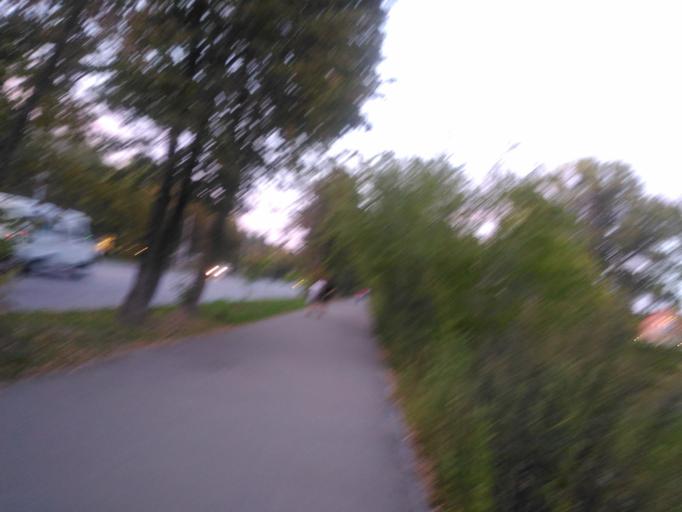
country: RU
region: Ulyanovsk
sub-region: Ulyanovskiy Rayon
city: Ulyanovsk
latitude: 54.3525
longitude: 48.5292
